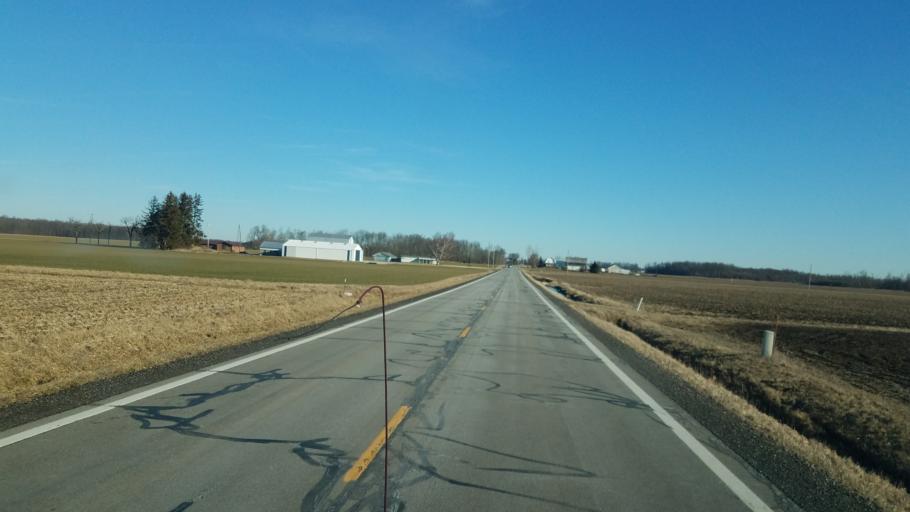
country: US
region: Ohio
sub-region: Crawford County
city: Crestline
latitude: 40.8051
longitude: -82.7308
